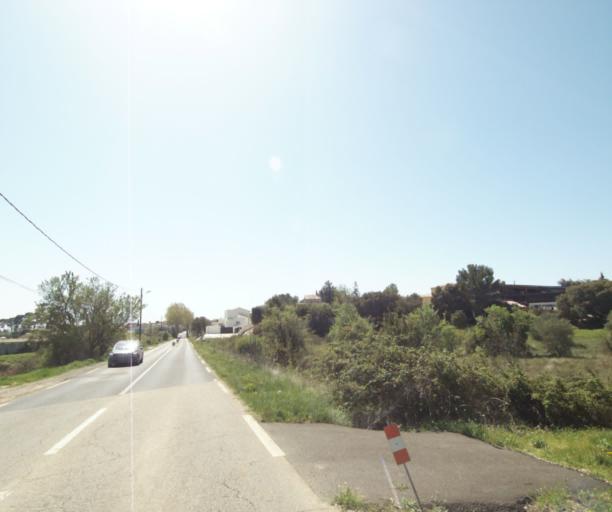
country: FR
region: Languedoc-Roussillon
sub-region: Departement de l'Herault
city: Restinclieres
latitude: 43.7273
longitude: 4.0418
